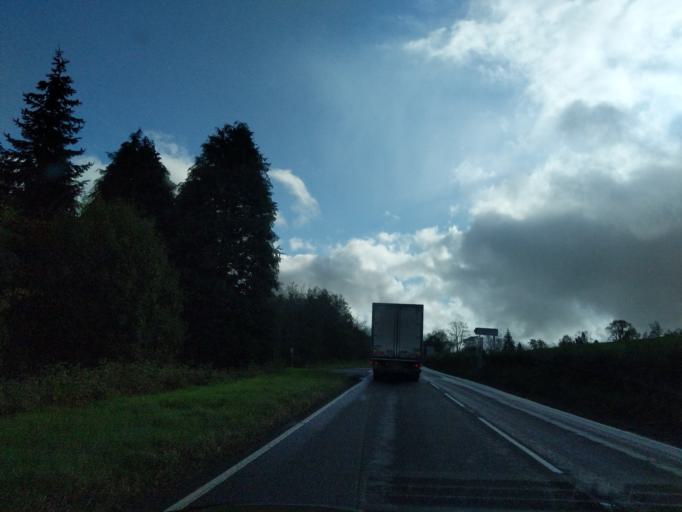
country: GB
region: Scotland
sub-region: Dumfries and Galloway
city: Moffat
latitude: 55.2851
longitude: -3.4449
